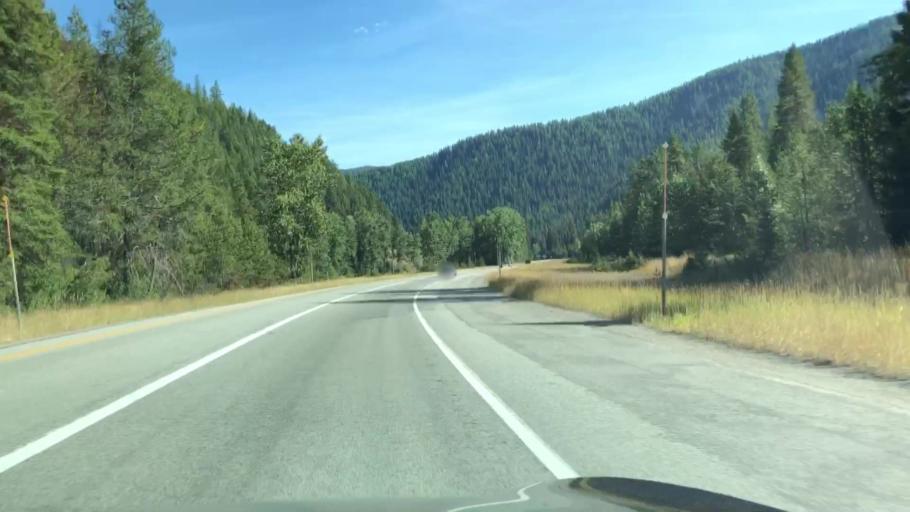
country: US
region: Idaho
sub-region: Shoshone County
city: Wallace
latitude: 47.4298
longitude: -115.6415
